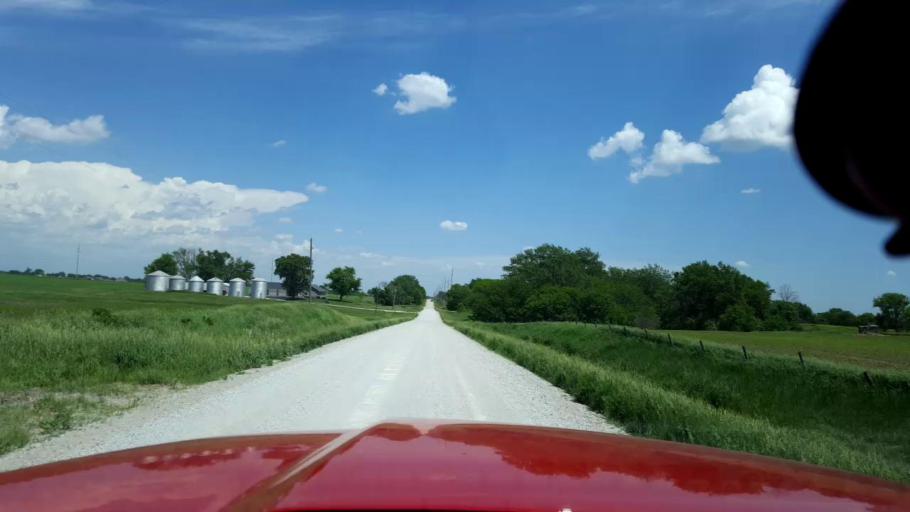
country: US
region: Iowa
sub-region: Boone County
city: Boone
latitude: 42.0493
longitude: -93.7627
